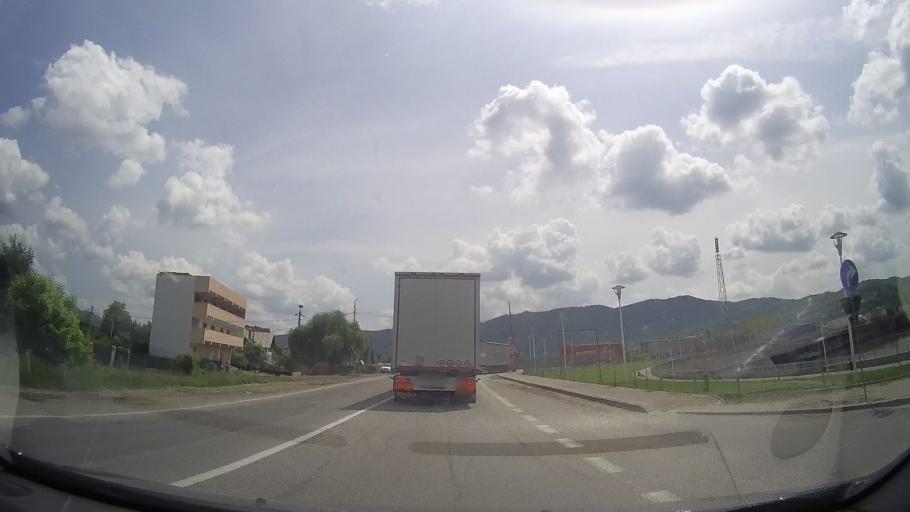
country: RO
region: Valcea
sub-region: Oras Calimanesti
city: Jiblea Veche
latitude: 45.2414
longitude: 24.3478
